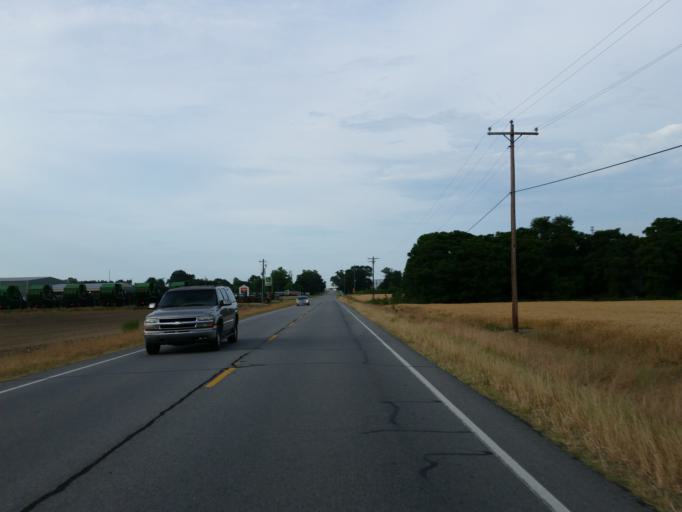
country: US
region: Georgia
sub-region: Dooly County
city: Unadilla
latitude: 32.2370
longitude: -83.7514
